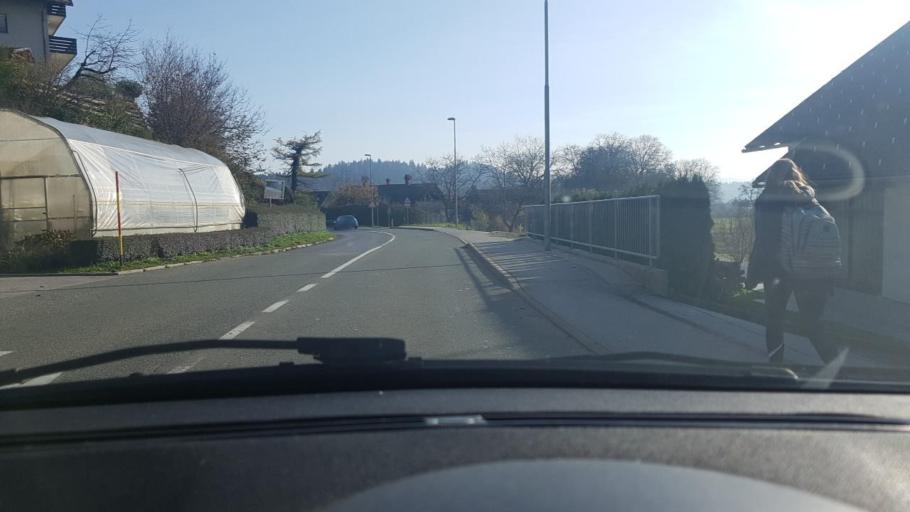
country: SI
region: Trzic
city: Bistrica pri Trzicu
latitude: 46.3395
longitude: 14.3006
